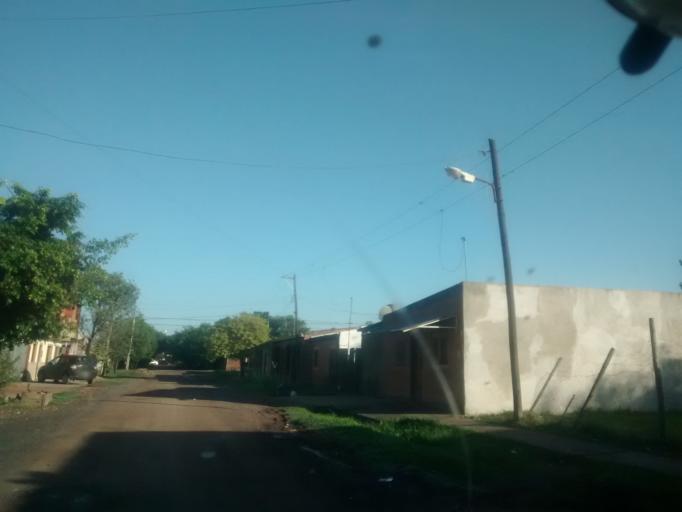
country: AR
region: Chaco
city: Resistencia
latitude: -27.4526
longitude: -59.0046
